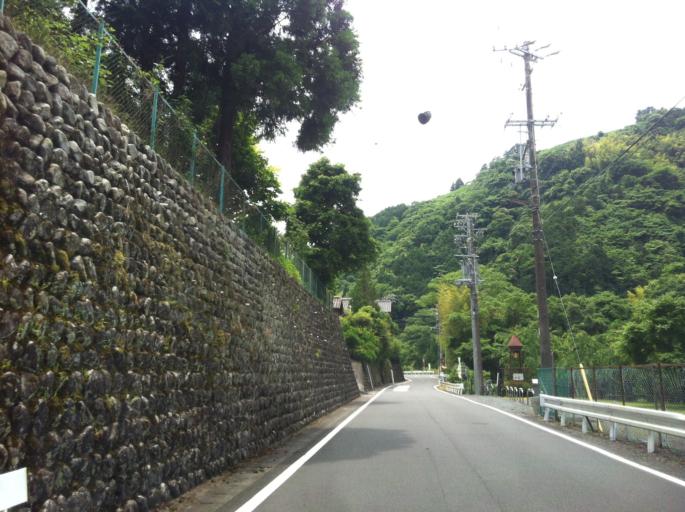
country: JP
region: Shizuoka
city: Shizuoka-shi
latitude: 35.0623
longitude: 138.4146
